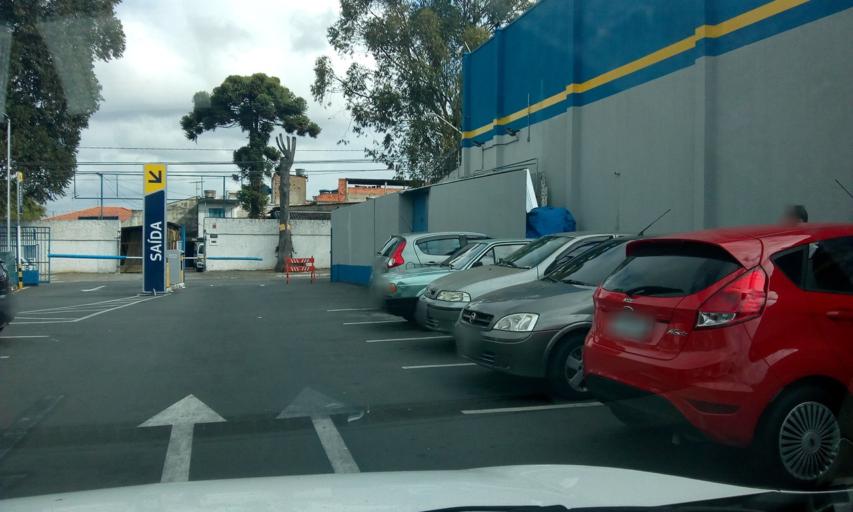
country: BR
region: Sao Paulo
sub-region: Diadema
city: Diadema
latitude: -23.6501
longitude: -46.6614
